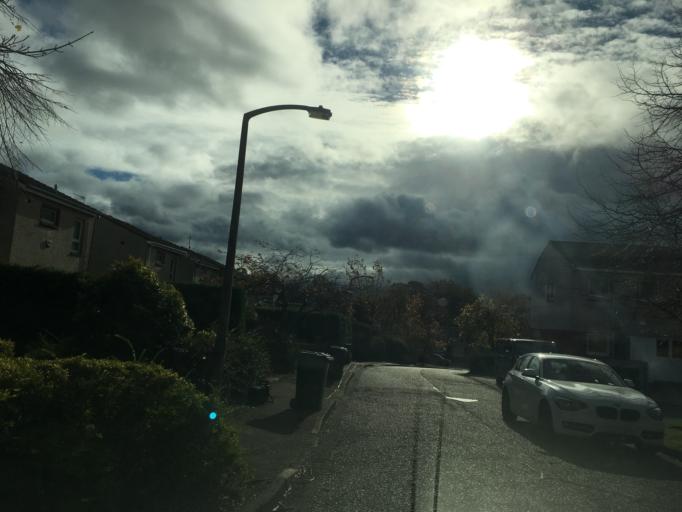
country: GB
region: Scotland
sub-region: Midlothian
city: Loanhead
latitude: 55.9043
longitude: -3.1724
